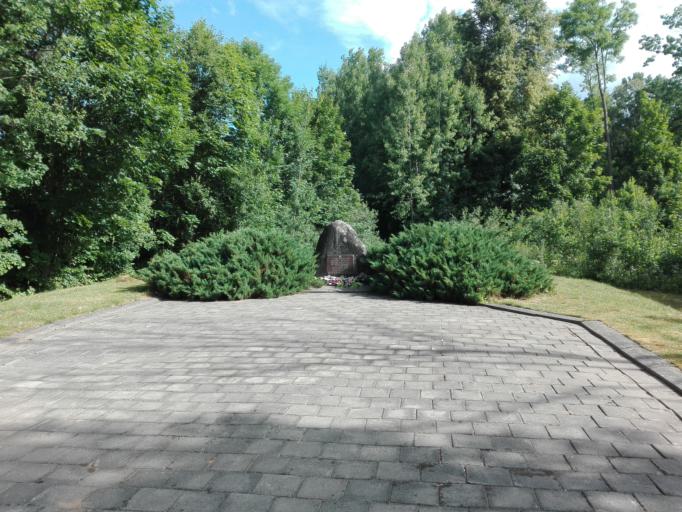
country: LT
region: Panevezys
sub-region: Birzai
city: Birzai
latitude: 56.2221
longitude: 24.7794
